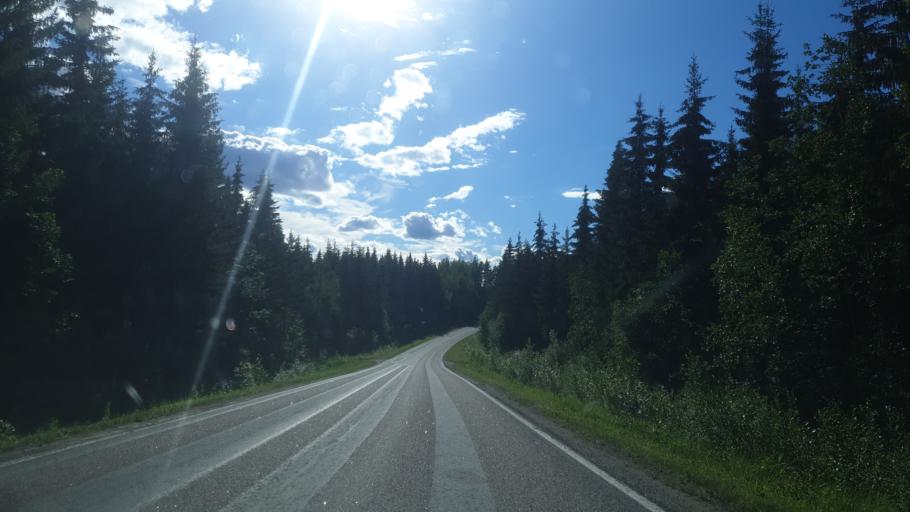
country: FI
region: Southern Savonia
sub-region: Mikkeli
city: Pertunmaa
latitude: 61.5224
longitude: 26.6465
